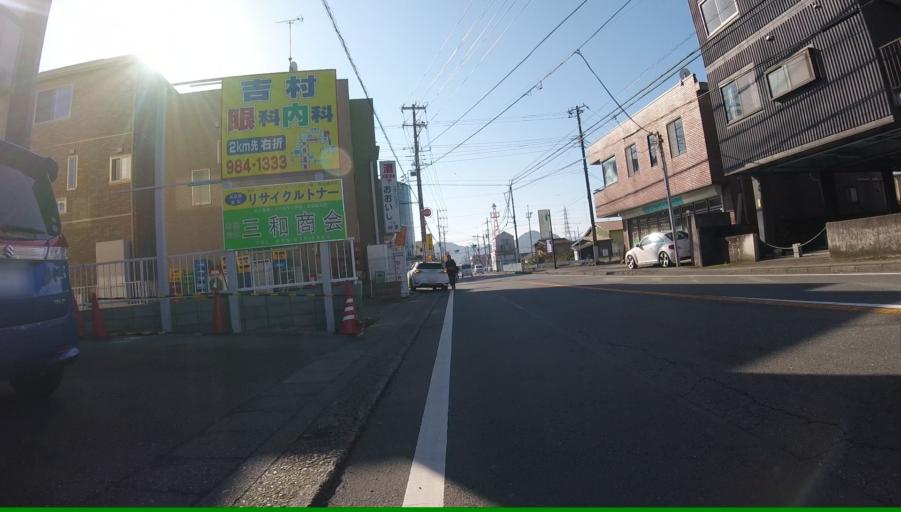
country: JP
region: Shizuoka
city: Mishima
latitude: 35.1038
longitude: 138.9160
